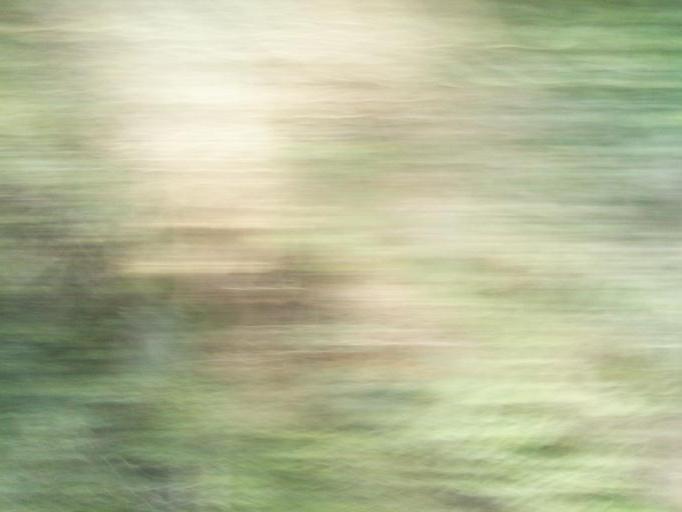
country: JP
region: Kochi
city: Nakamura
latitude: 32.9943
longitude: 132.9648
